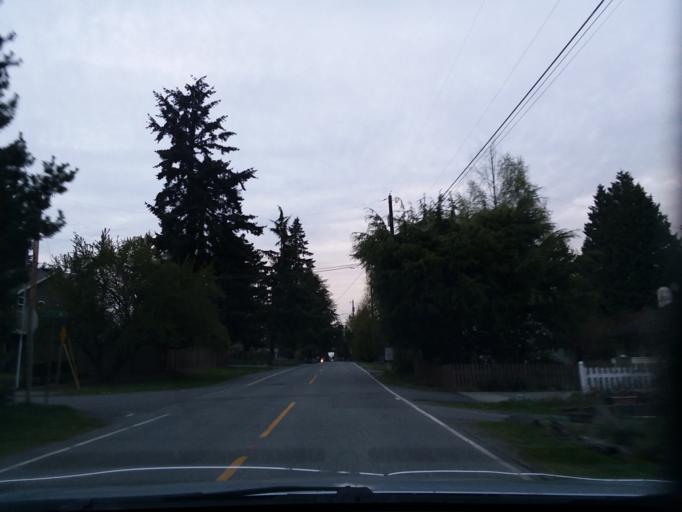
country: US
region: Washington
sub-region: Snohomish County
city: Esperance
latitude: 47.8002
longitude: -122.3410
